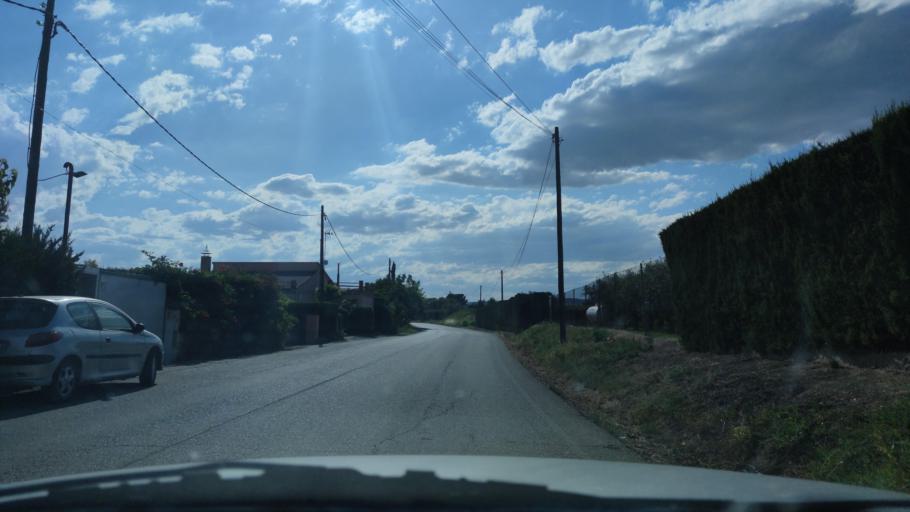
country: ES
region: Catalonia
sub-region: Provincia de Lleida
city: Alpicat
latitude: 41.6240
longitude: 0.5667
